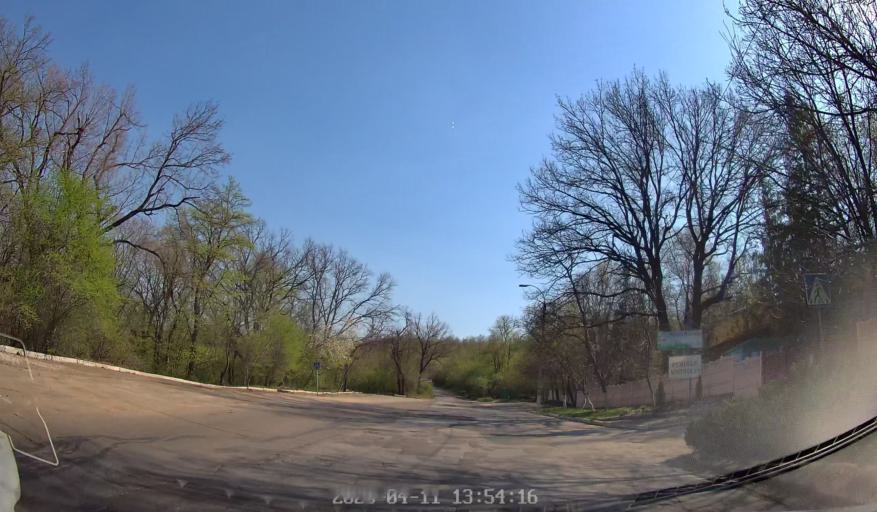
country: MD
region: Chisinau
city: Vadul lui Voda
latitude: 47.0754
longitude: 29.1007
